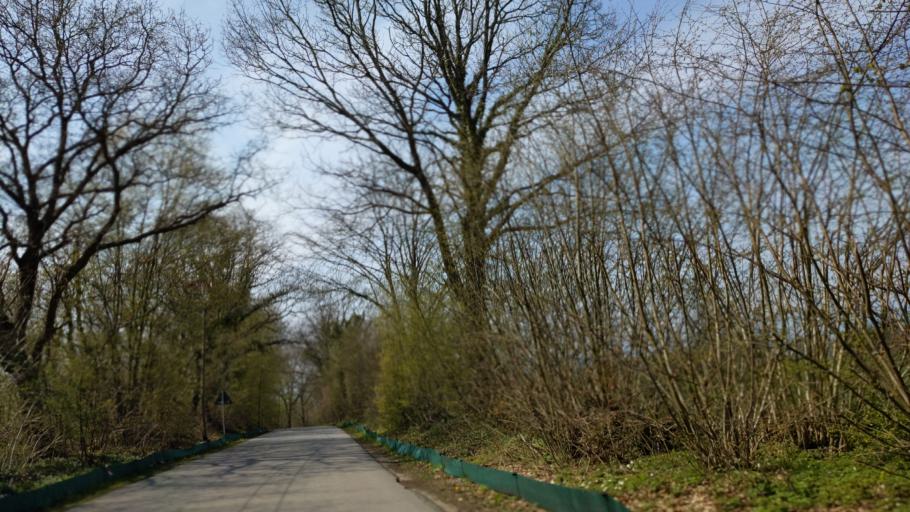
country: DE
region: Schleswig-Holstein
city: Ratekau
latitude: 53.9316
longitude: 10.7941
